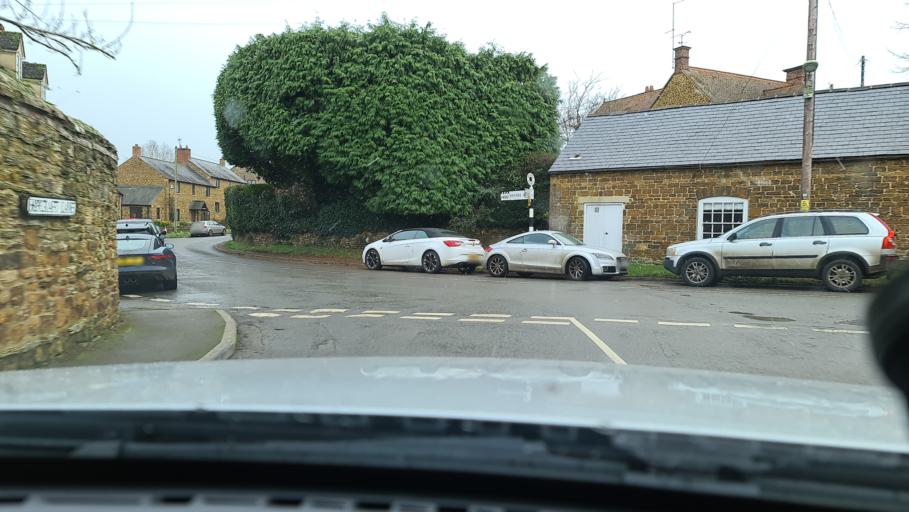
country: GB
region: England
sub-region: Oxfordshire
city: Deddington
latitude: 51.9796
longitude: -1.3196
